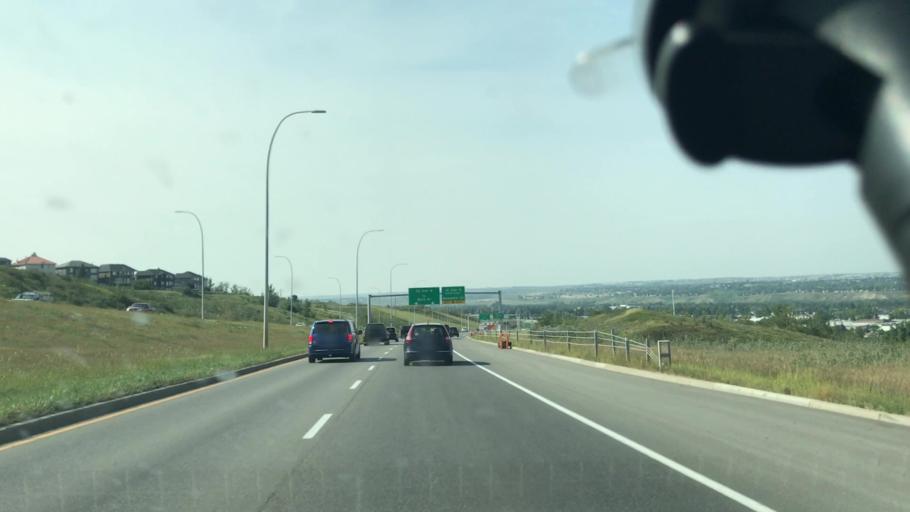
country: CA
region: Alberta
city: Calgary
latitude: 51.0714
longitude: -114.1821
